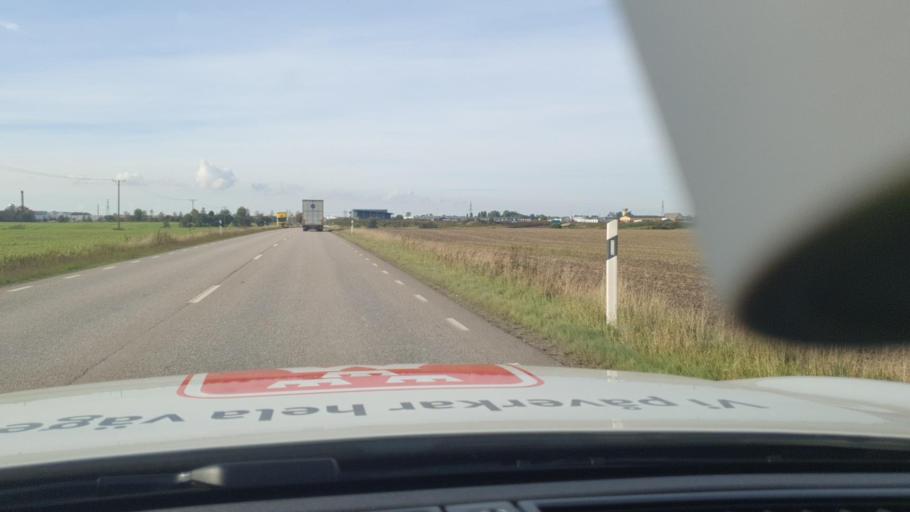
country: SE
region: Skane
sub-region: Angelholms Kommun
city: Munka-Ljungby
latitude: 56.2533
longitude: 12.9242
